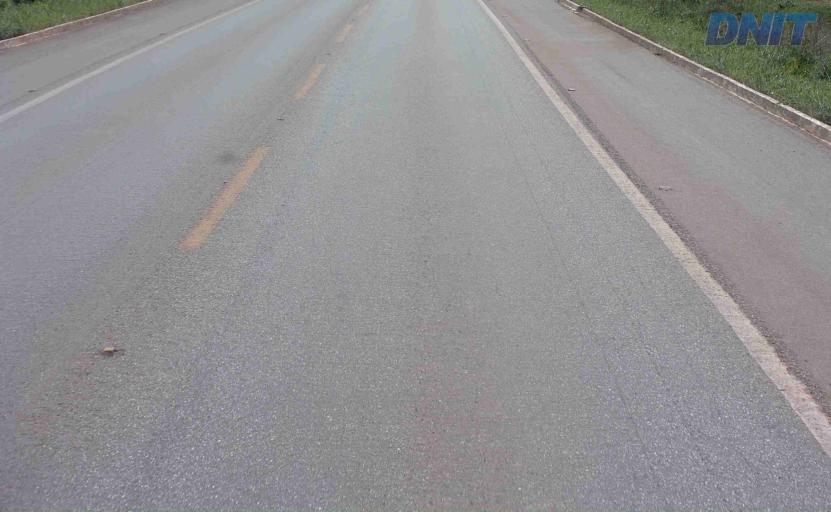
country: BR
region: Goias
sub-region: Barro Alto
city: Barro Alto
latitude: -15.2077
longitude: -48.7072
